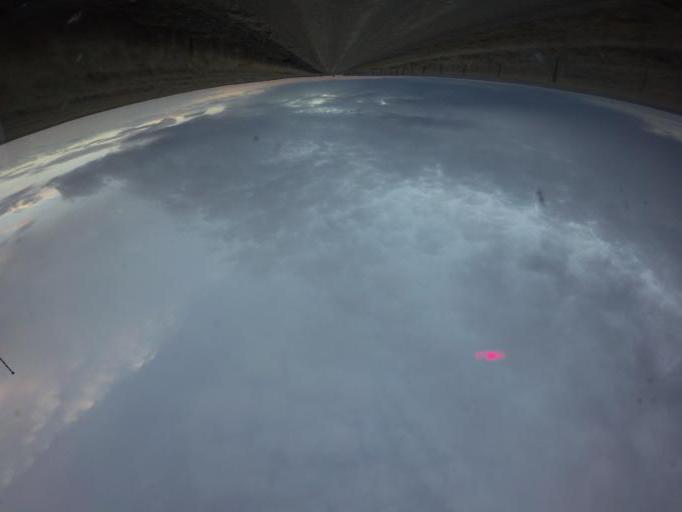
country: US
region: Montana
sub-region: Yellowstone County
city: Laurel
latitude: 45.9439
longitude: -108.7995
